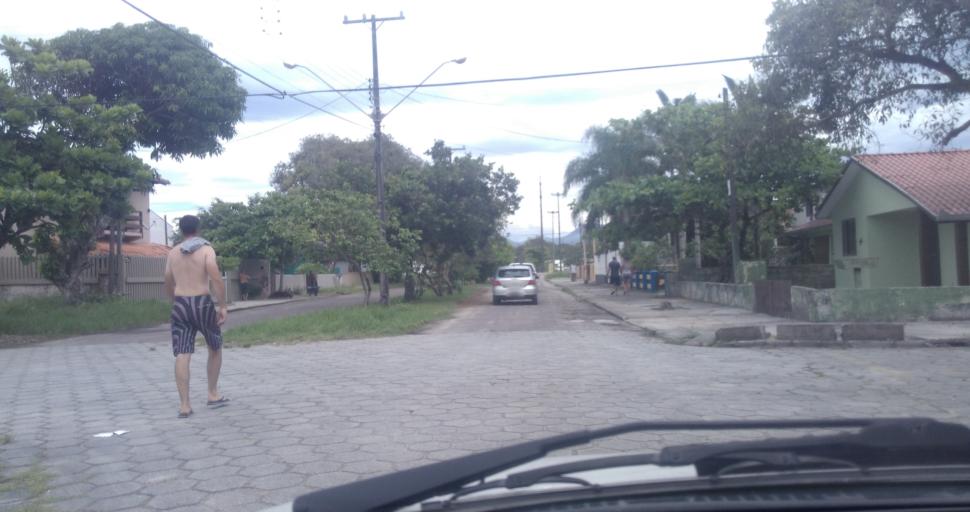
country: BR
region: Parana
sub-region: Pontal Do Parana
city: Pontal do Parana
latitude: -25.7612
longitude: -48.5082
